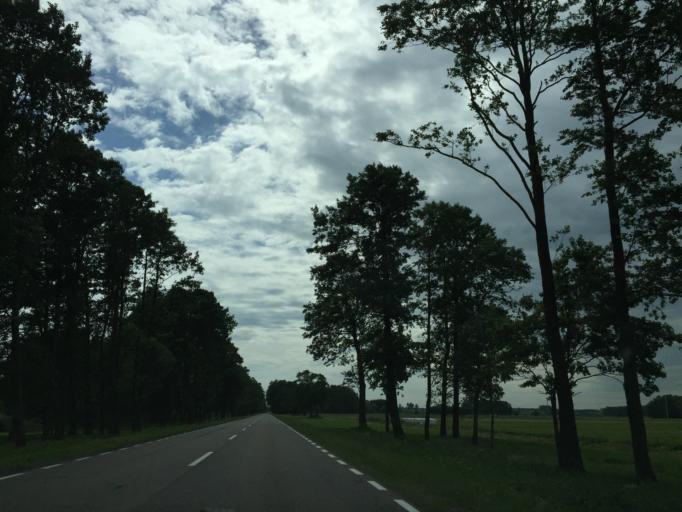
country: PL
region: Podlasie
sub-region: Powiat bielski
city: Bocki
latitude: 52.6328
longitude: 23.0182
